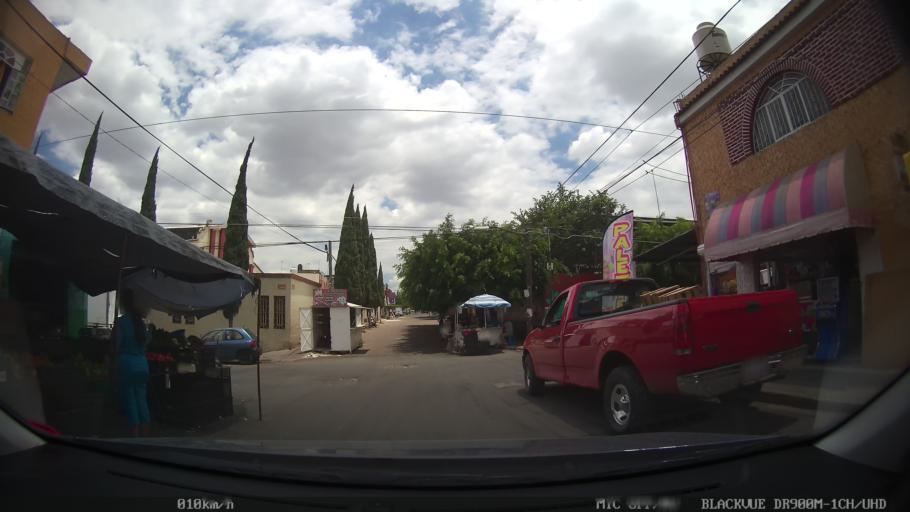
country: MX
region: Jalisco
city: Tlaquepaque
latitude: 20.6347
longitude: -103.2685
